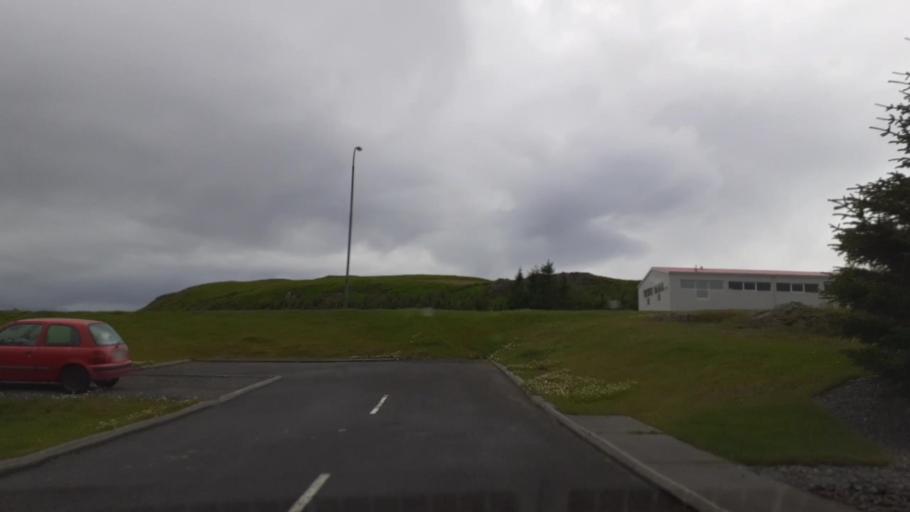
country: IS
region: East
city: Egilsstadir
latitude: 65.7538
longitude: -14.8363
